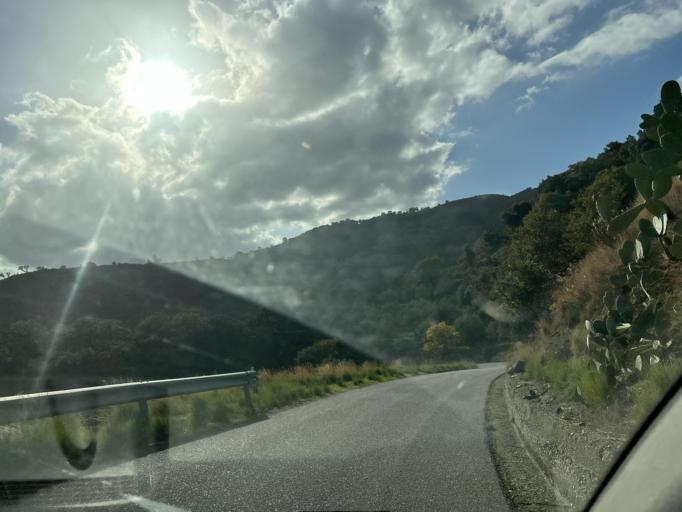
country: IT
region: Calabria
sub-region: Provincia di Catanzaro
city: Montepaone
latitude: 38.7180
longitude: 16.5107
